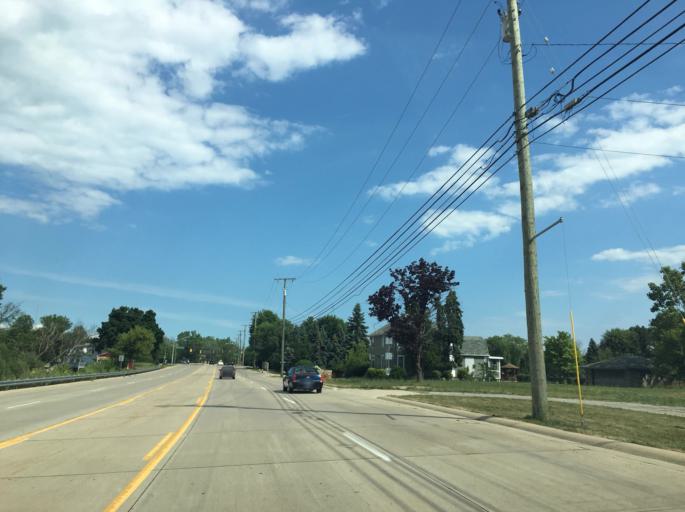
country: US
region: Michigan
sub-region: Macomb County
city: Clinton
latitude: 42.6065
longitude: -82.9204
